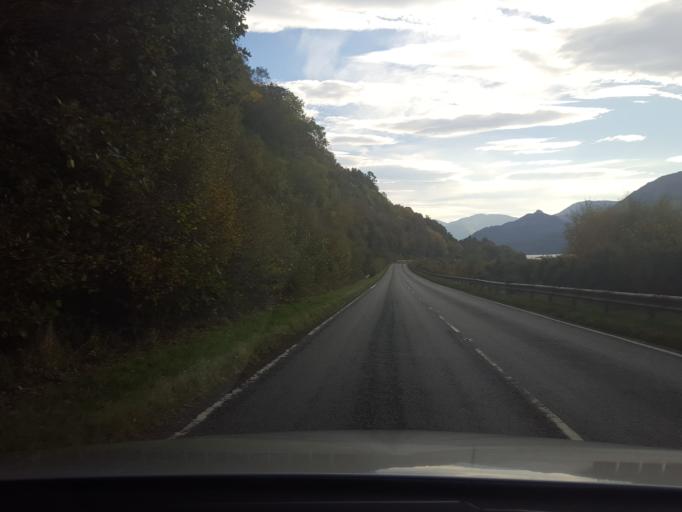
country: GB
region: Scotland
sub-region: Highland
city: Fort William
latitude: 57.2559
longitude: -5.4801
